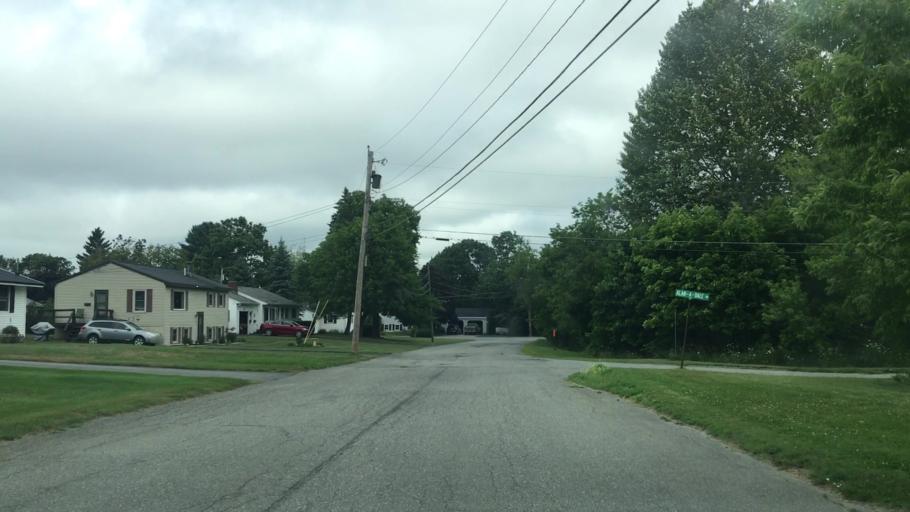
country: US
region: Maine
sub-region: Penobscot County
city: Brewer
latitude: 44.7731
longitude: -68.7696
